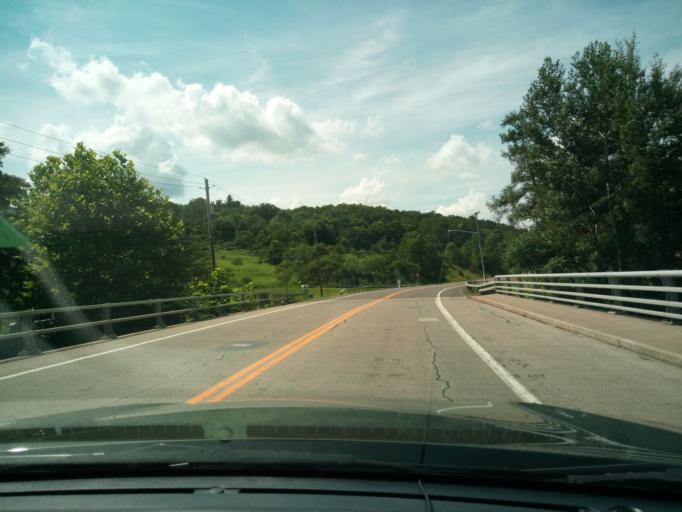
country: US
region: New York
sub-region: Chemung County
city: Southport
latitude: 42.0171
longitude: -76.7314
